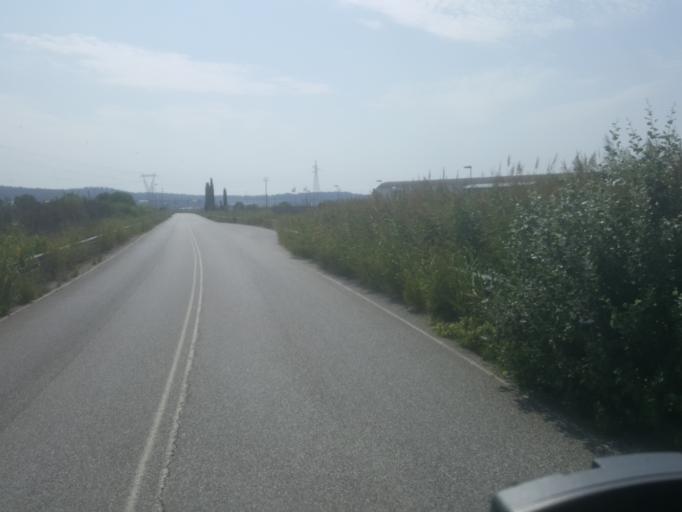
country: IT
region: Tuscany
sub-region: Provincia di Livorno
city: Guasticce
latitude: 43.6034
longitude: 10.4039
